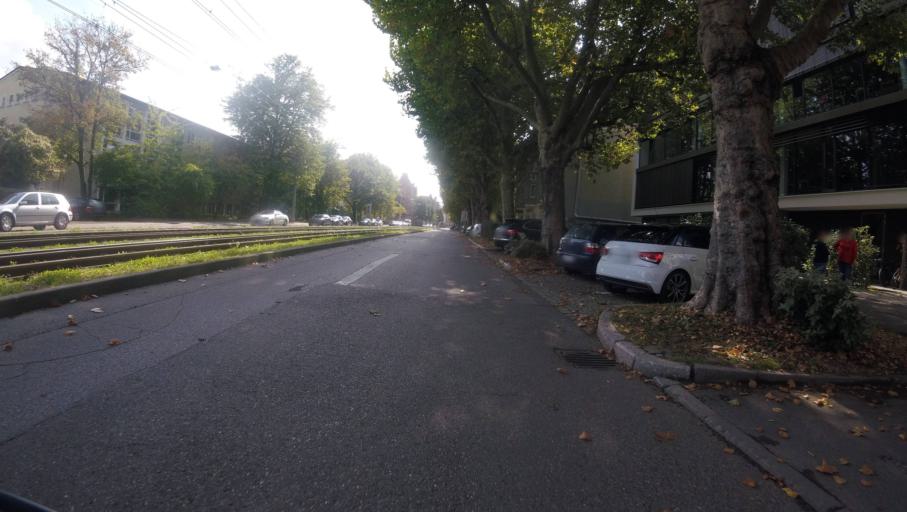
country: DE
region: Baden-Wuerttemberg
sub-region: Regierungsbezirk Stuttgart
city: Stuttgart
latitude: 48.8008
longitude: 9.1899
